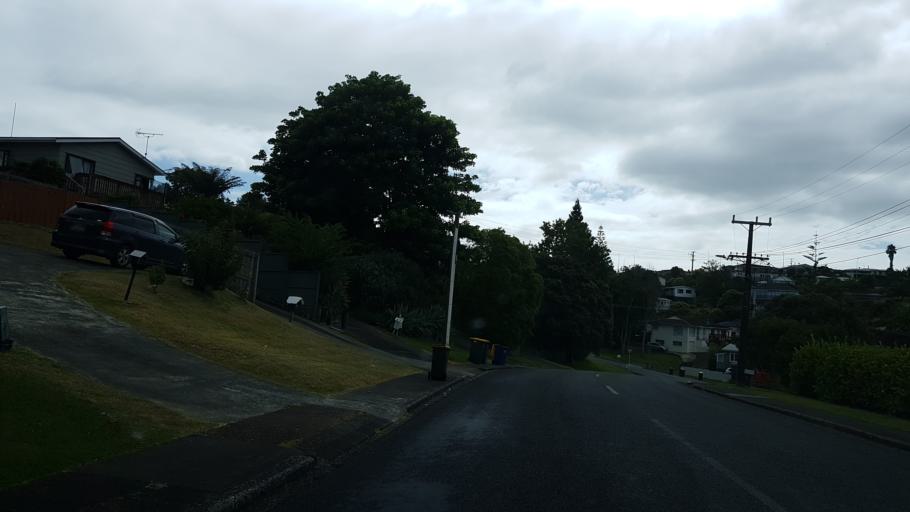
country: NZ
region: Auckland
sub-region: Auckland
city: North Shore
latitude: -36.7737
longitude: 174.7242
